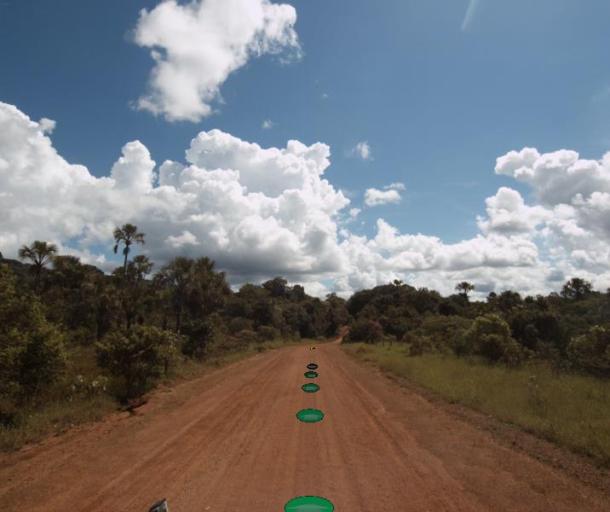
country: BR
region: Goias
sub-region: Pirenopolis
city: Pirenopolis
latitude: -15.7809
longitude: -48.8276
